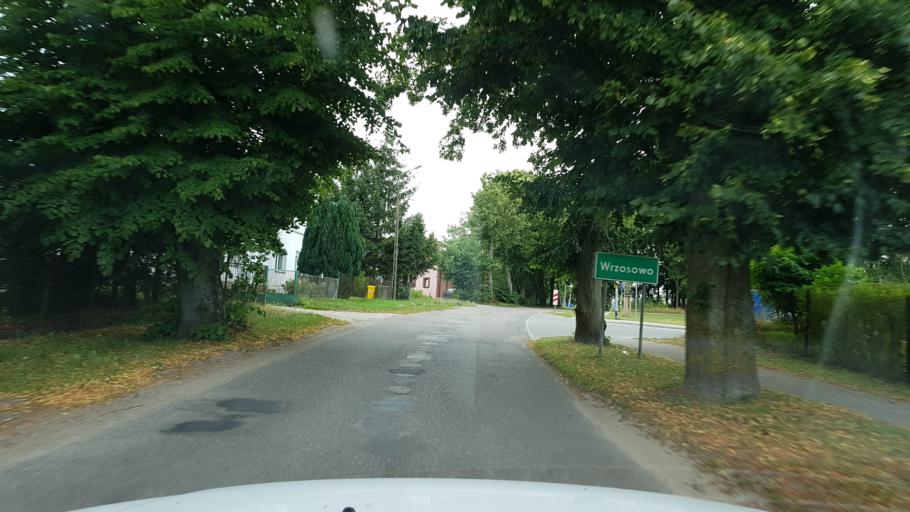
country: PL
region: West Pomeranian Voivodeship
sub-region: Powiat bialogardzki
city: Karlino
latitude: 54.1158
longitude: 15.8391
